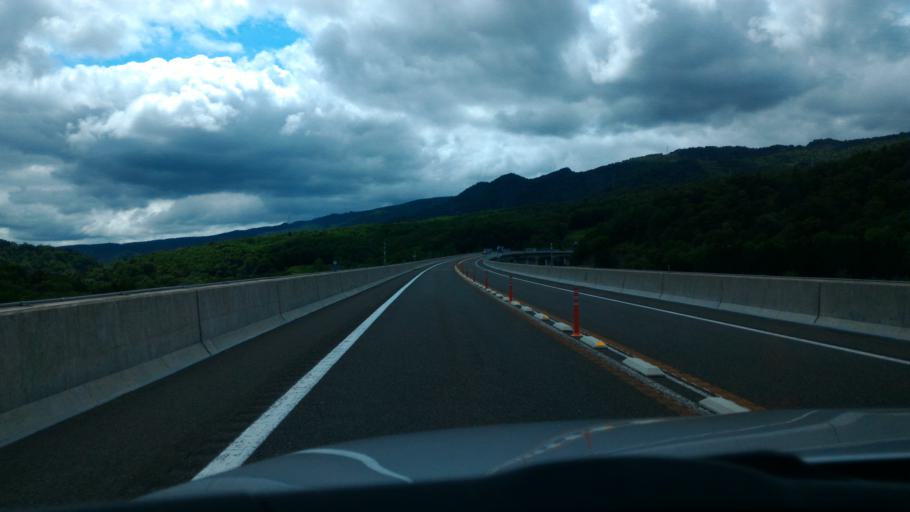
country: JP
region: Hokkaido
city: Shimo-furano
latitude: 42.9526
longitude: 142.3156
